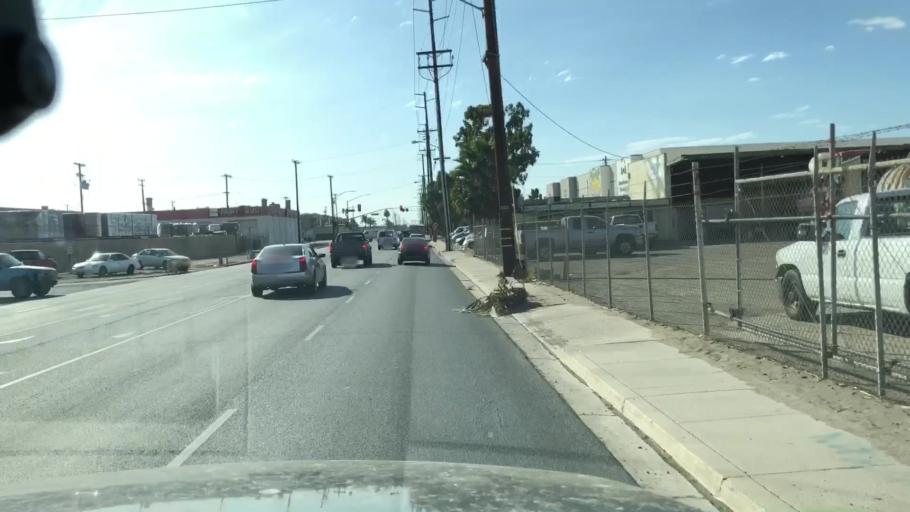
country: US
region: California
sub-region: Ventura County
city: Oxnard
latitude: 34.1900
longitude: -119.1692
